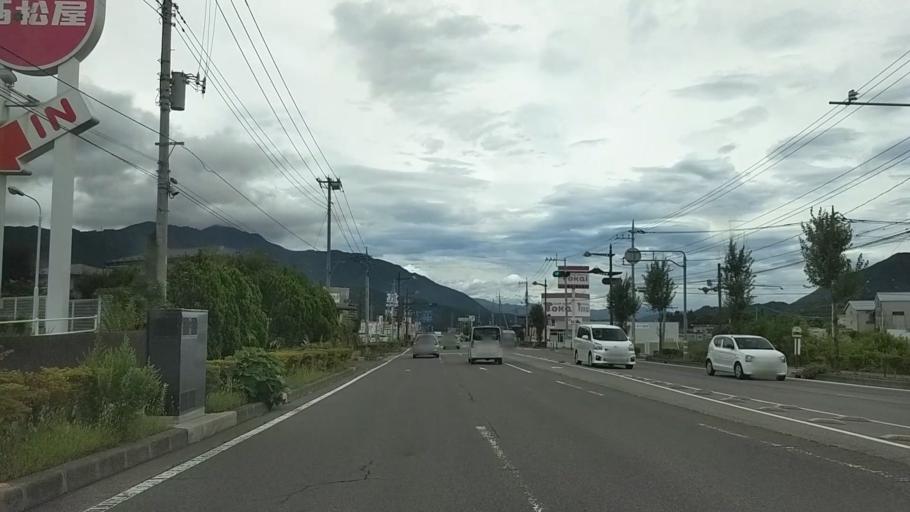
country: JP
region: Yamanashi
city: Fujikawaguchiko
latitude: 35.4791
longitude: 138.8094
